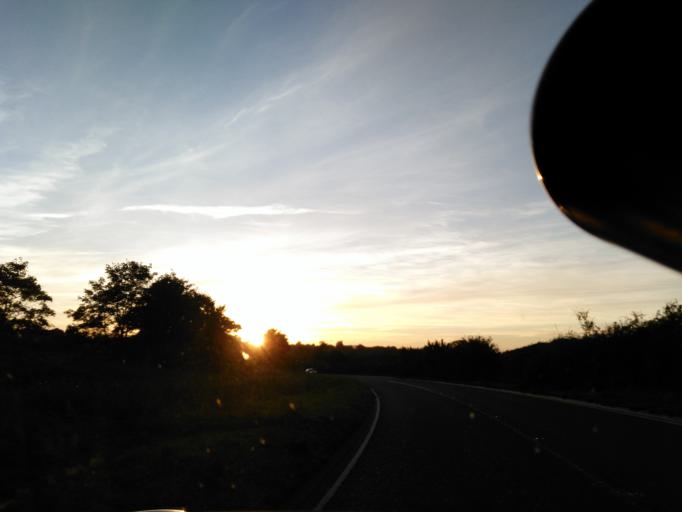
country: GB
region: England
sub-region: Wiltshire
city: Seend
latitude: 51.3521
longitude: -2.0546
